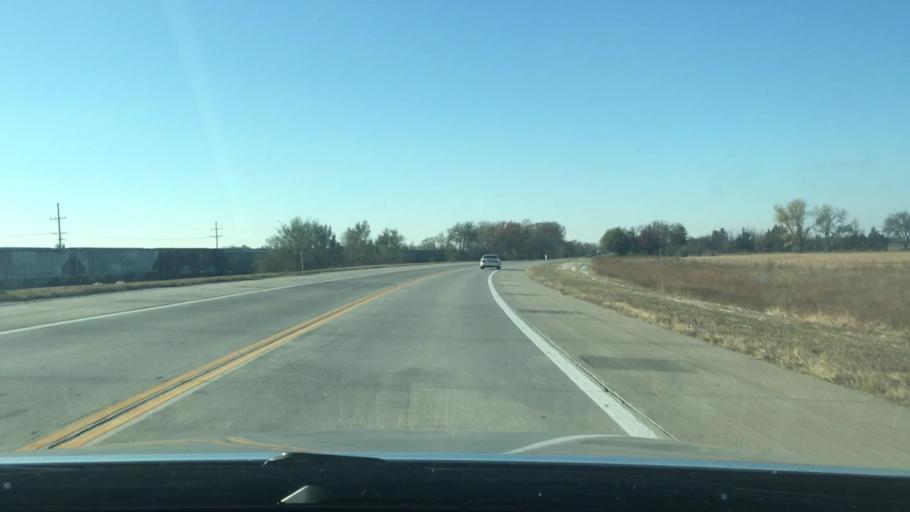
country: US
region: Kansas
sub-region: Reno County
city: Nickerson
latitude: 38.1051
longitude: -98.0216
